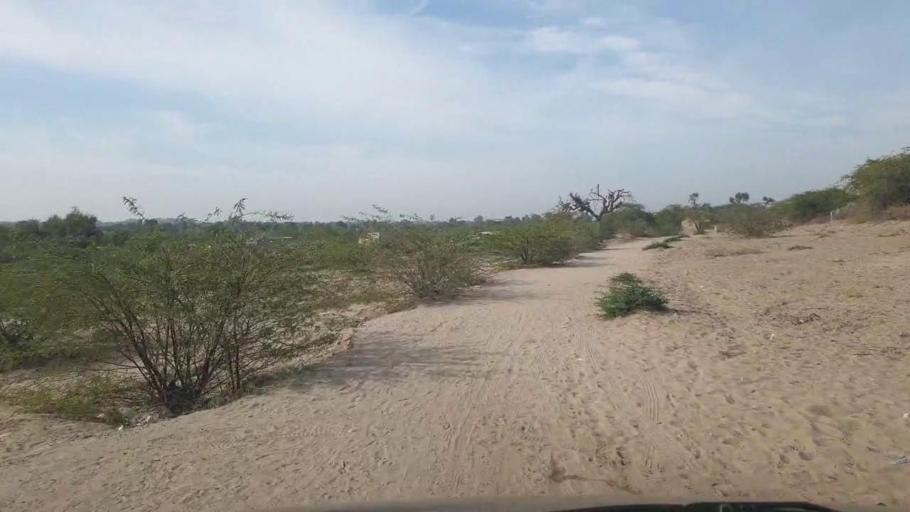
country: PK
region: Sindh
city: Umarkot
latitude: 25.3084
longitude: 69.7065
